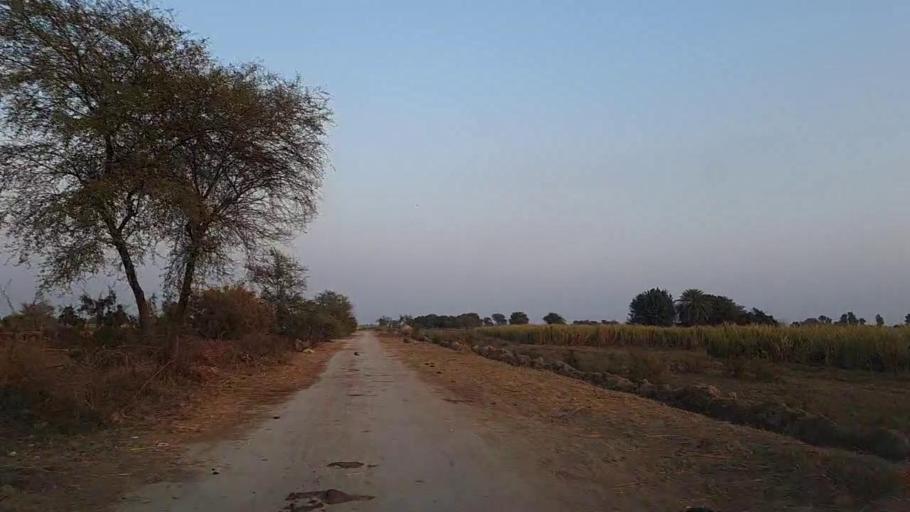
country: PK
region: Sindh
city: Jam Sahib
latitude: 26.3090
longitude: 68.5815
